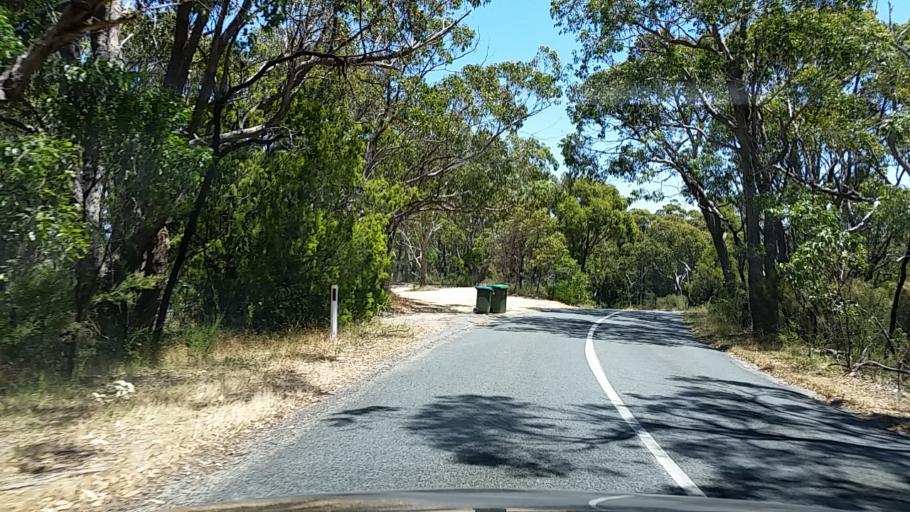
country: AU
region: South Australia
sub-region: Adelaide Hills
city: Crafers
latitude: -34.9889
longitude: 138.6862
